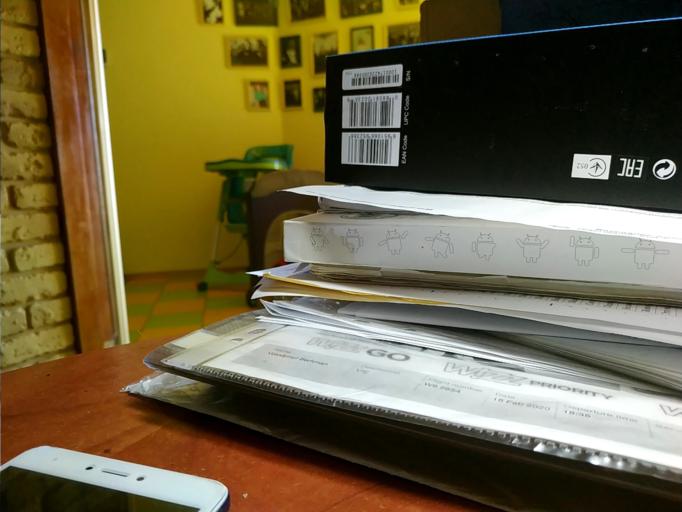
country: RU
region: Novgorod
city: Kholm
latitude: 59.2433
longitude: 32.8795
